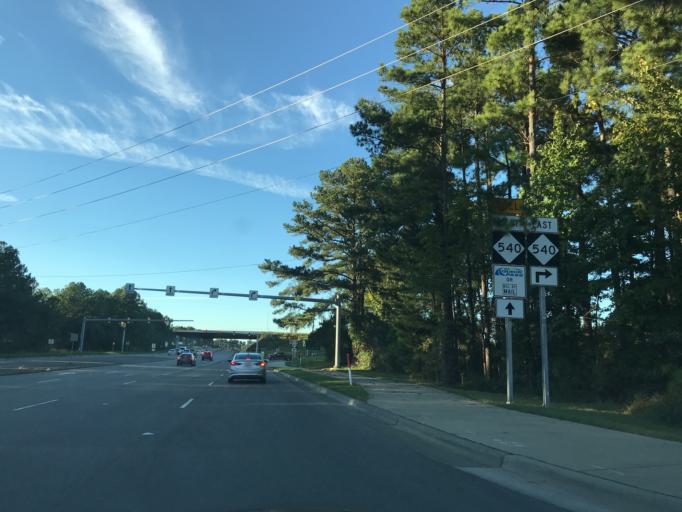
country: US
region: North Carolina
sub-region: Wake County
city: Morrisville
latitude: 35.8587
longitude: -78.8432
